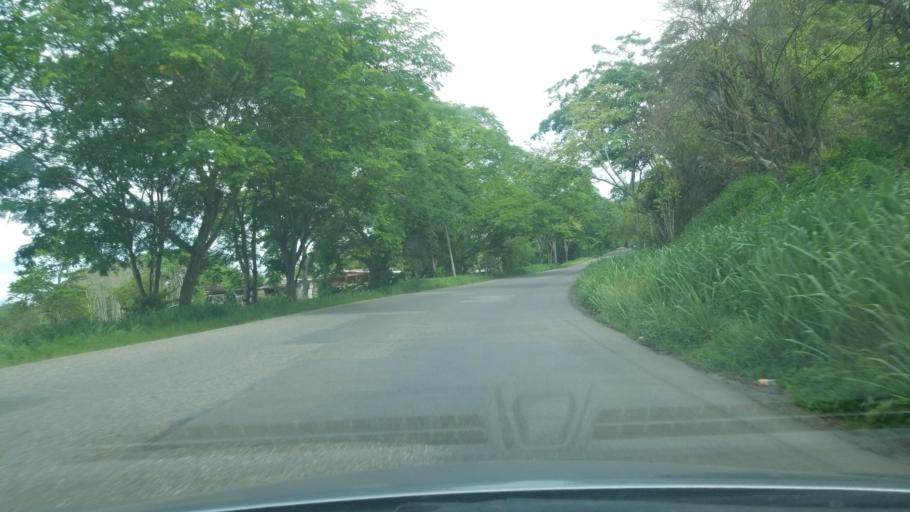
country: HN
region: Santa Barbara
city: Camalote
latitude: 15.3220
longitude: -88.3137
